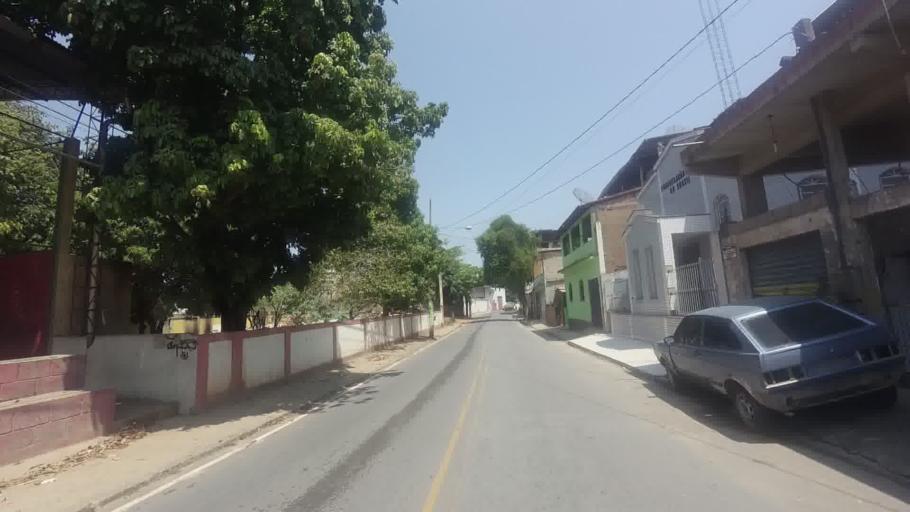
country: BR
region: Espirito Santo
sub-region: Cachoeiro De Itapemirim
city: Cachoeiro de Itapemirim
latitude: -20.8521
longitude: -41.0950
